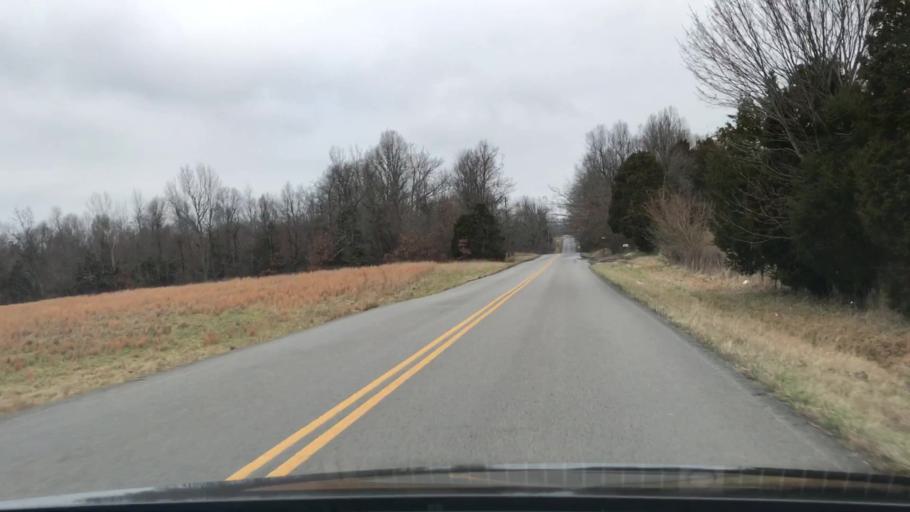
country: US
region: Kentucky
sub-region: Muhlenberg County
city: Morehead
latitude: 37.3204
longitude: -87.2181
